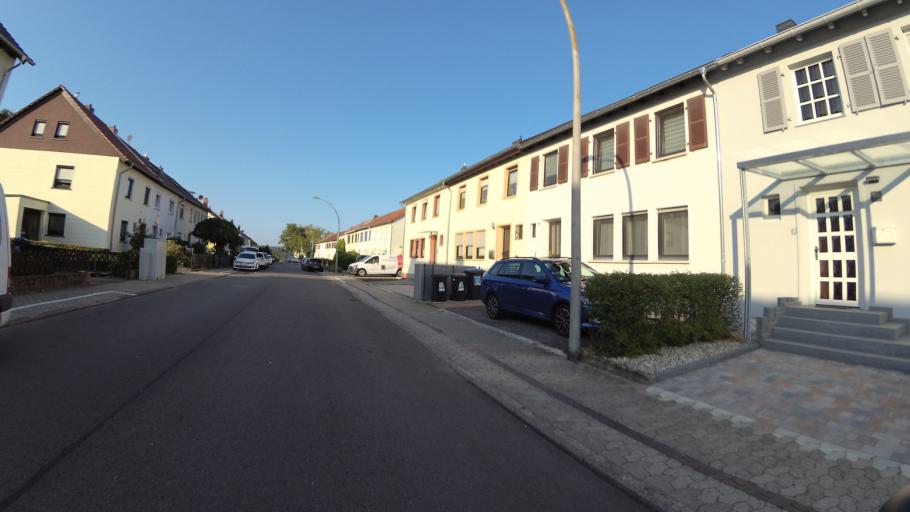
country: DE
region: Saarland
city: Sankt Ingbert
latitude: 49.2685
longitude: 7.1033
